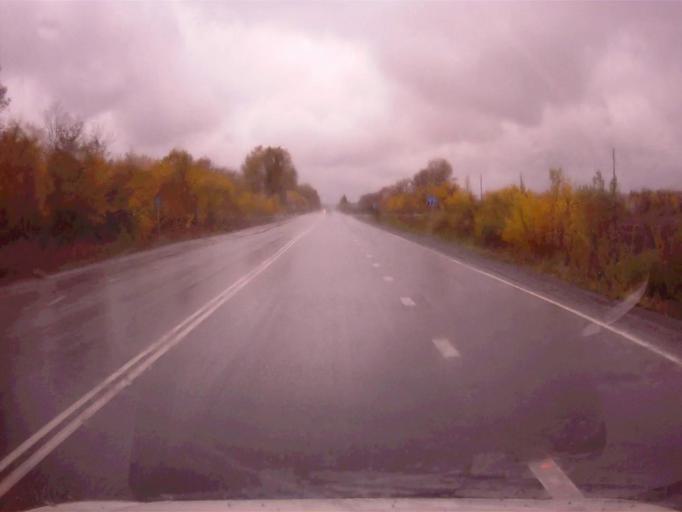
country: RU
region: Chelyabinsk
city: Argayash
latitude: 55.4334
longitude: 60.9829
